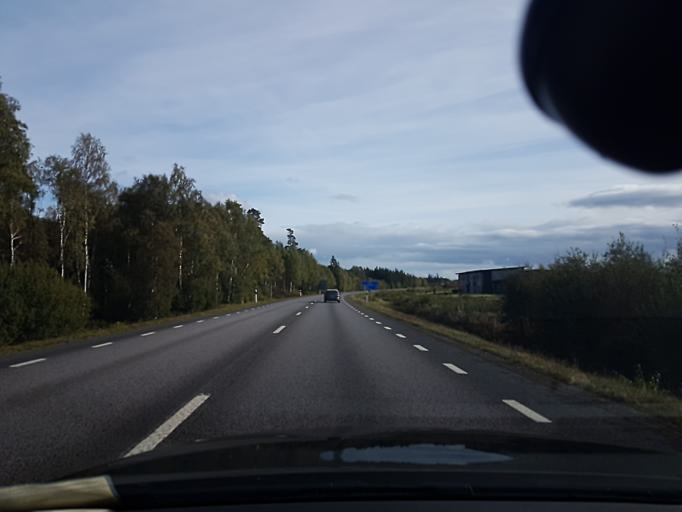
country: SE
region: Joenkoeping
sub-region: Varnamo Kommun
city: Varnamo
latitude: 57.1629
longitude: 14.0781
